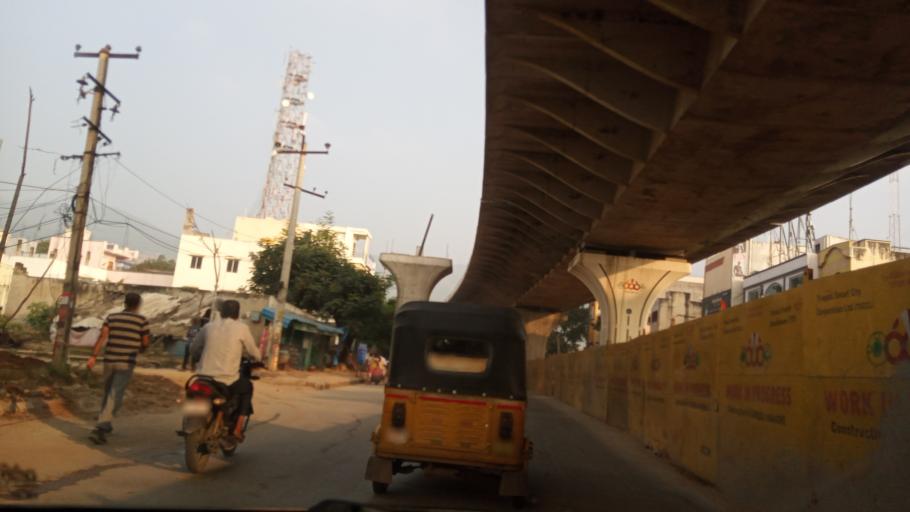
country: IN
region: Andhra Pradesh
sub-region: Chittoor
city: Akkarampalle
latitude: 13.6449
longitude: 79.4275
